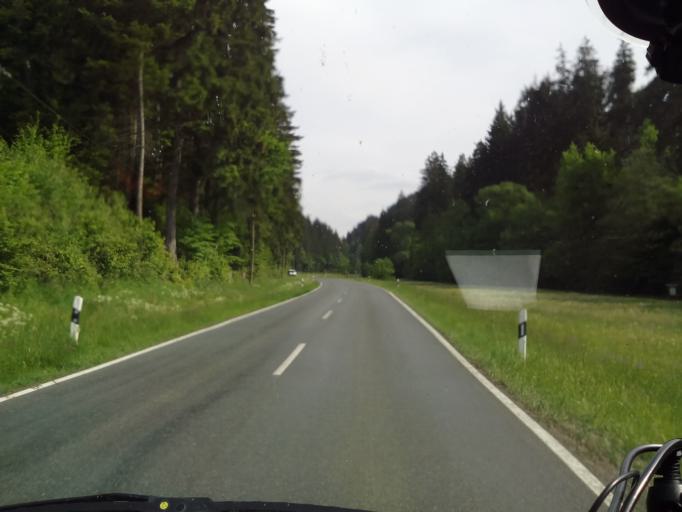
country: DE
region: Bavaria
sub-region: Upper Franconia
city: Steinwiesen
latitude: 50.3004
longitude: 11.4466
